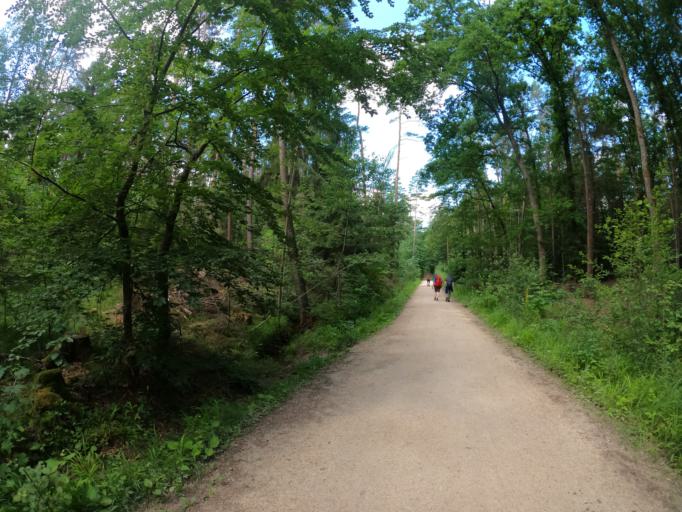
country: DE
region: Bavaria
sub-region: Upper Franconia
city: Memmelsdorf
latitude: 49.8957
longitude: 10.9415
